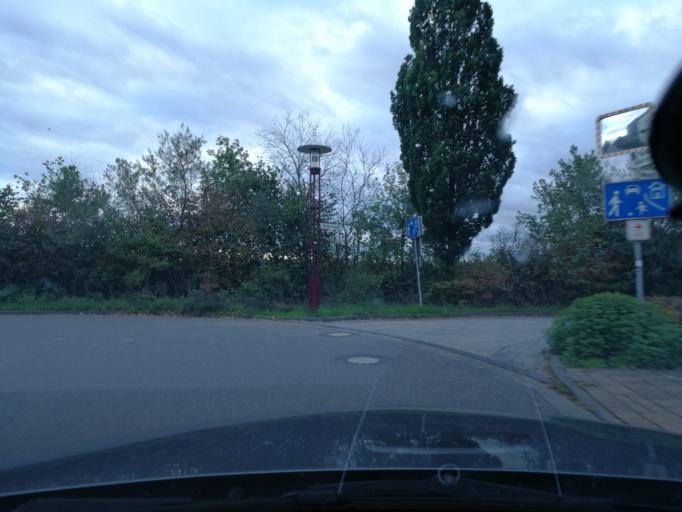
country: DE
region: North Rhine-Westphalia
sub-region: Regierungsbezirk Dusseldorf
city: Willich
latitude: 51.2548
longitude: 6.5366
